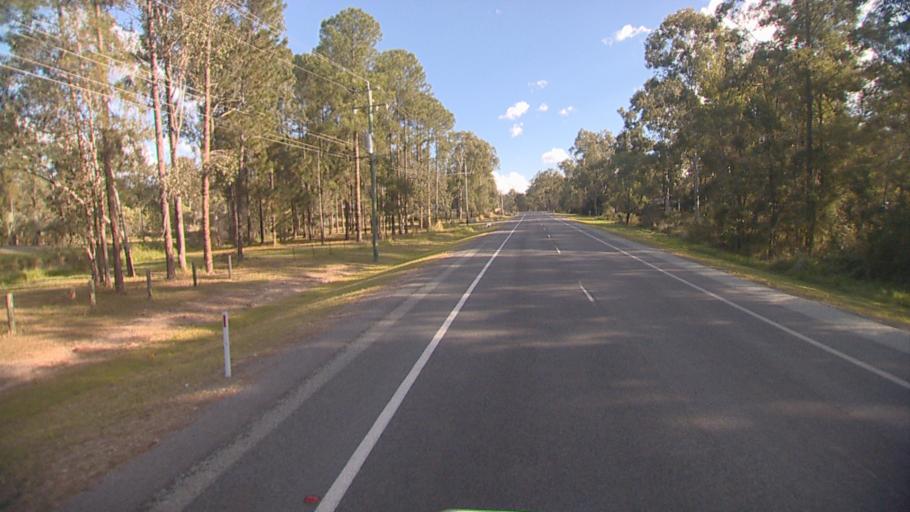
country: AU
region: Queensland
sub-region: Ipswich
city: Springfield Lakes
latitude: -27.7222
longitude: 152.9607
